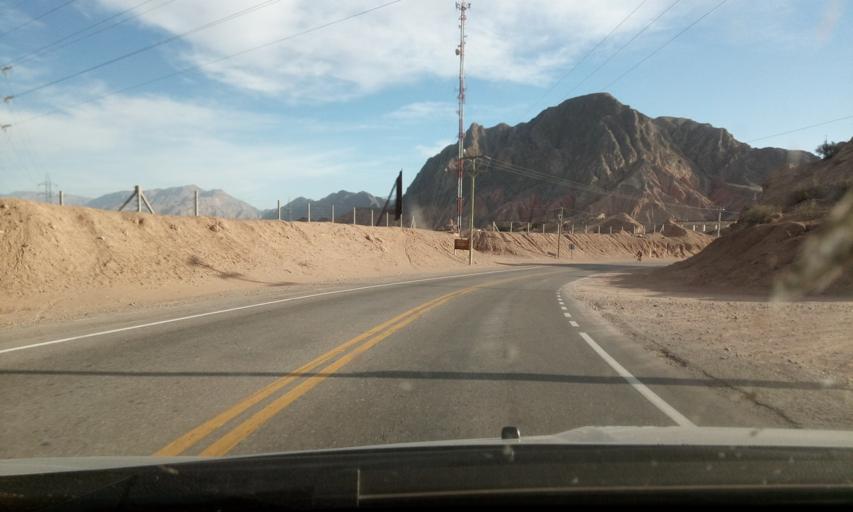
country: AR
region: San Juan
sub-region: Departamento de Rivadavia
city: Rivadavia
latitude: -31.4738
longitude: -68.6446
